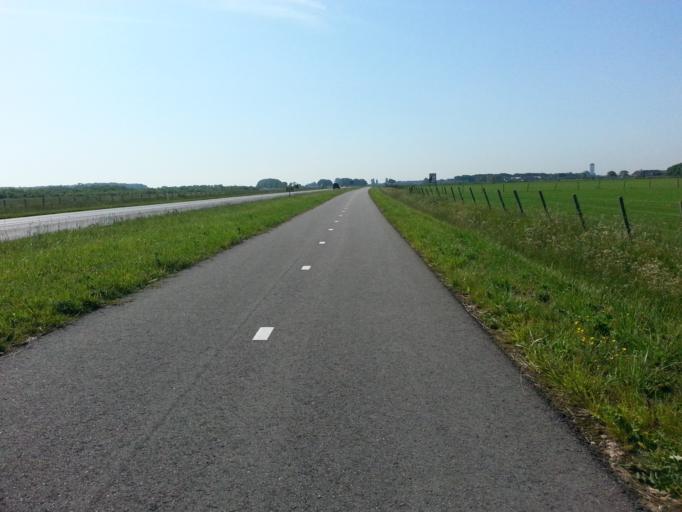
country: NL
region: Utrecht
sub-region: Gemeente Utrechtse Heuvelrug
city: Driebergen-Rijsenburg
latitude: 52.0190
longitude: 5.2605
